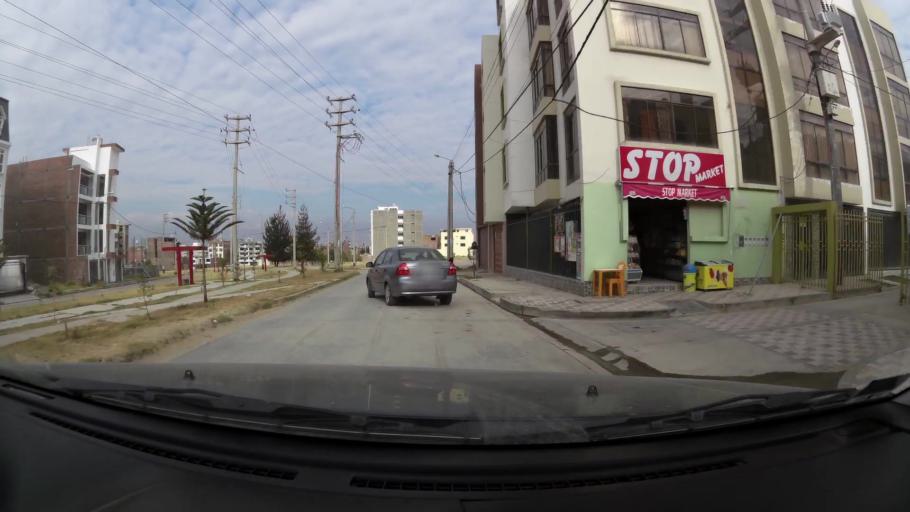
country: PE
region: Junin
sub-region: Provincia de Huancayo
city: Huancayo
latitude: -12.0478
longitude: -75.1886
